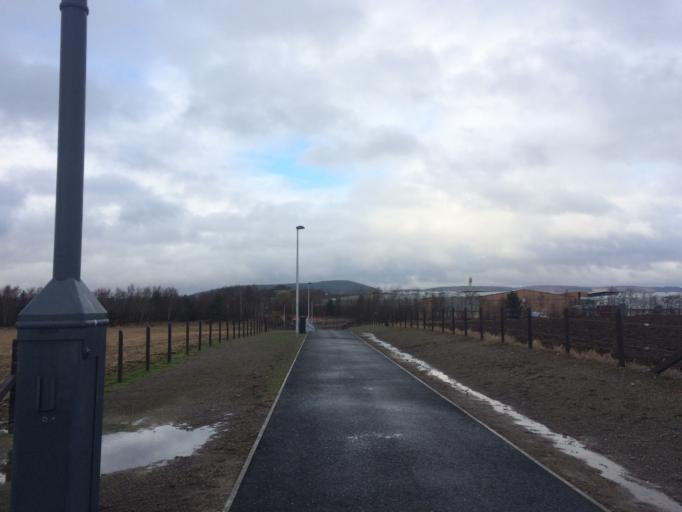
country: GB
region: Scotland
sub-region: Highland
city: Inverness
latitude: 57.4783
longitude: -4.1766
